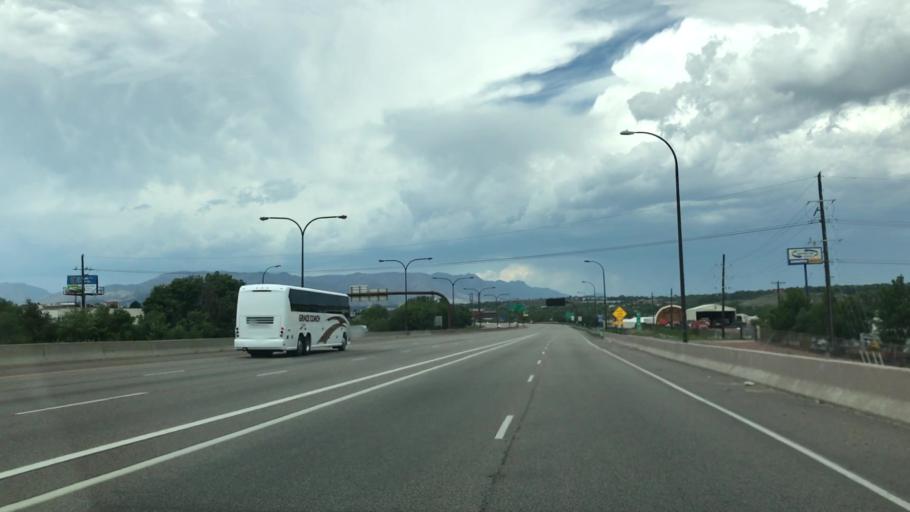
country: US
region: Colorado
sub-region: El Paso County
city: Stratmoor
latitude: 38.7990
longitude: -104.7987
